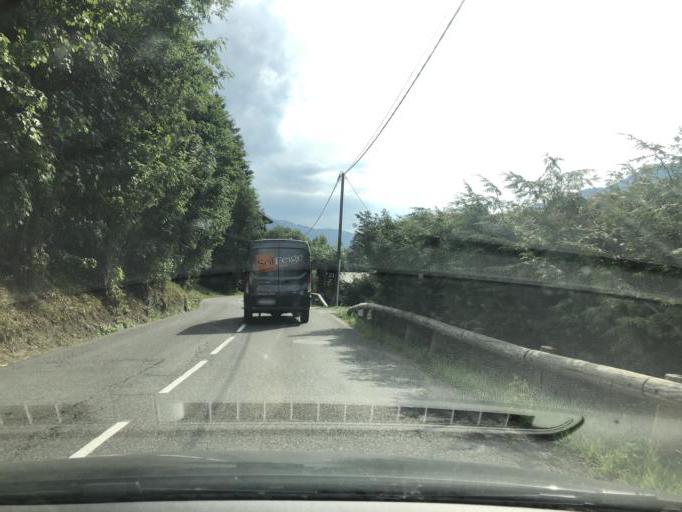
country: FR
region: Rhone-Alpes
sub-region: Departement de la Haute-Savoie
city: Megeve
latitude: 45.8609
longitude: 6.6275
